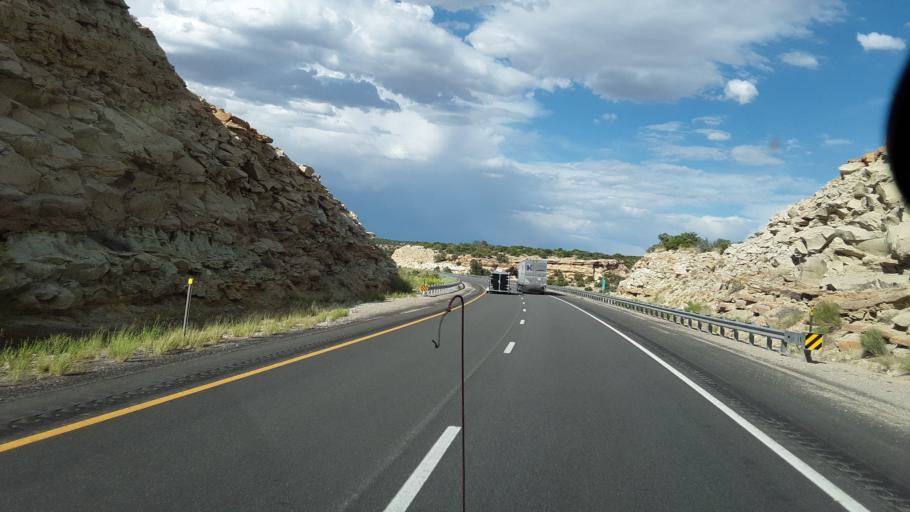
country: US
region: Utah
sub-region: Emery County
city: Ferron
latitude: 38.8530
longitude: -110.8753
